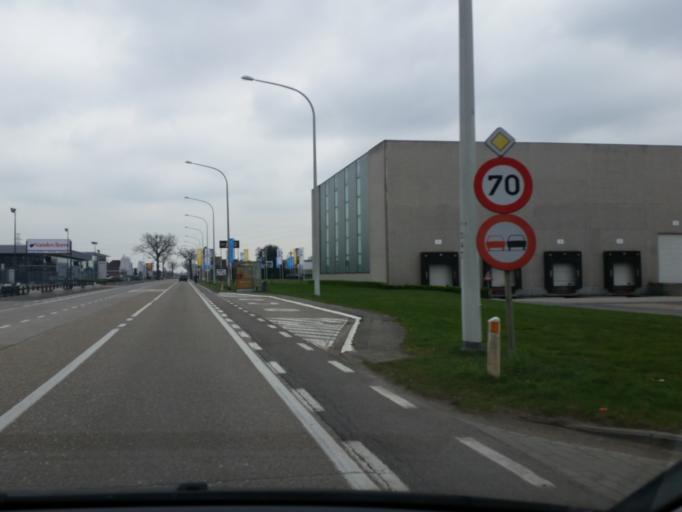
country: BE
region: Flanders
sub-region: Provincie Vlaams-Brabant
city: Boortmeerbeek
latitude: 50.9664
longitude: 4.5762
